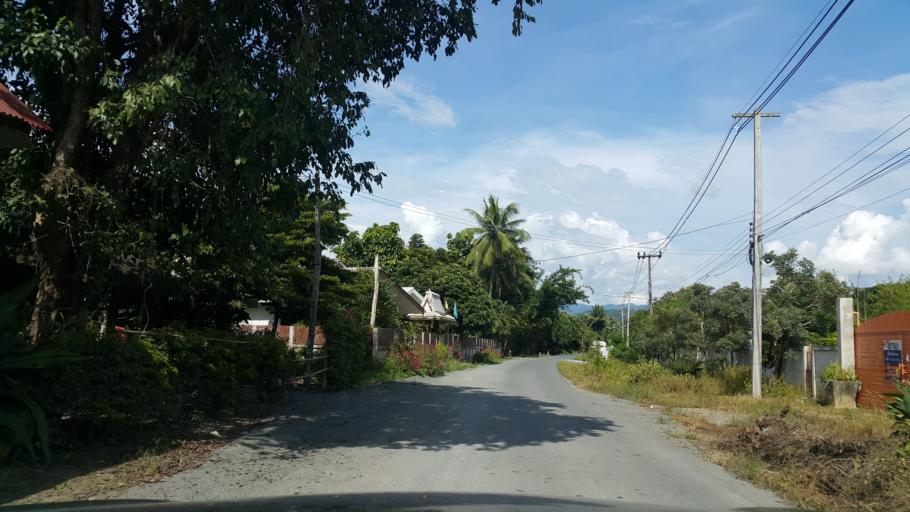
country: TH
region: Chiang Mai
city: Mae On
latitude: 18.8333
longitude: 99.1994
